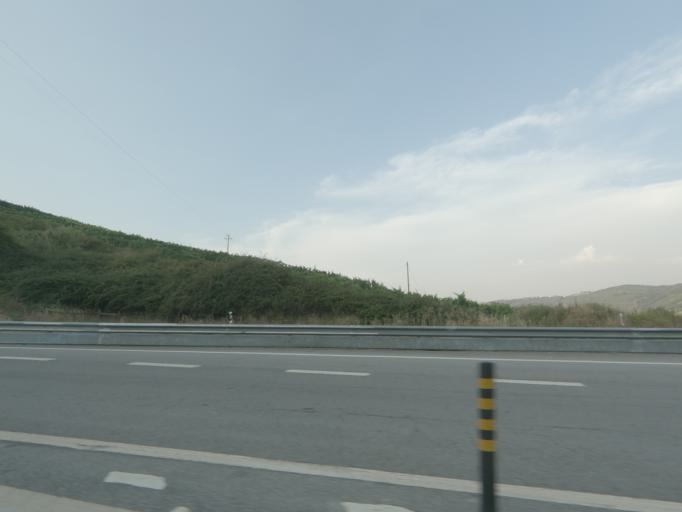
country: PT
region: Vila Real
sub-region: Peso da Regua
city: Peso da Regua
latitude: 41.1691
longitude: -7.7728
